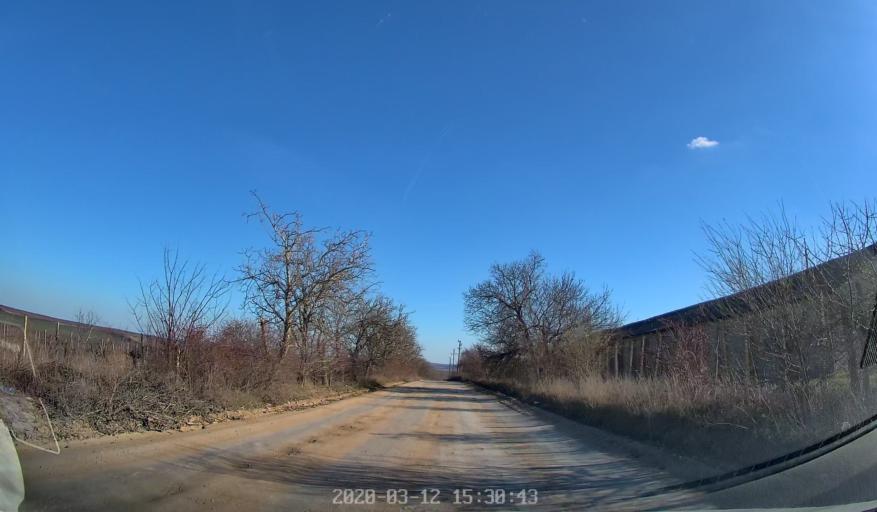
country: MD
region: Chisinau
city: Ciorescu
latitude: 47.1599
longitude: 28.9398
